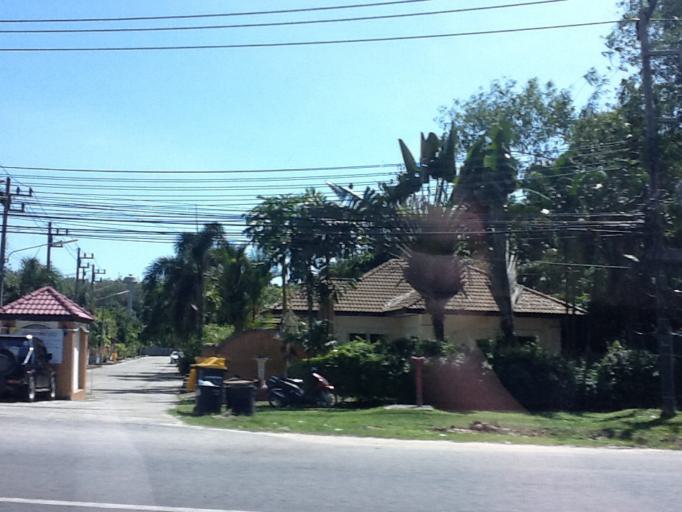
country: TH
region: Phuket
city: Ban Ko Kaeo
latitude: 7.9961
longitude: 98.3894
